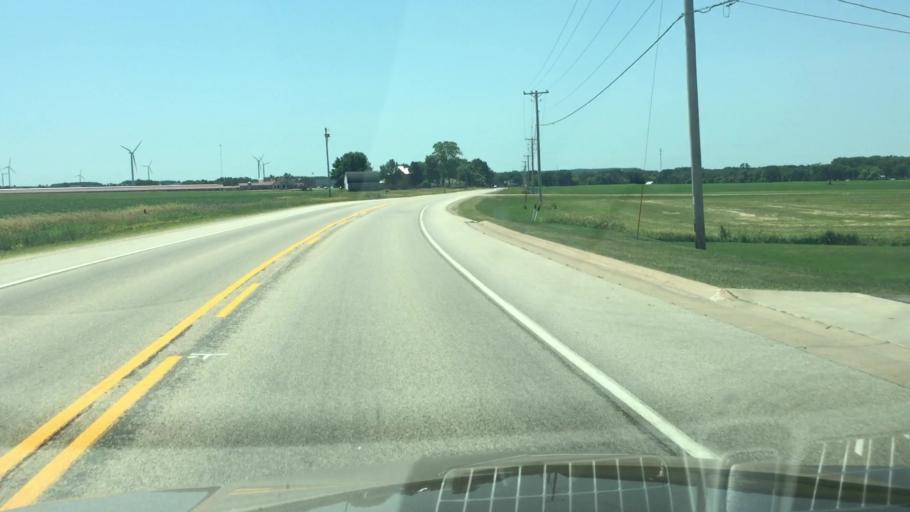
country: US
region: Wisconsin
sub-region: Fond du Lac County
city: Saint Peter
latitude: 43.9272
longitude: -88.3059
